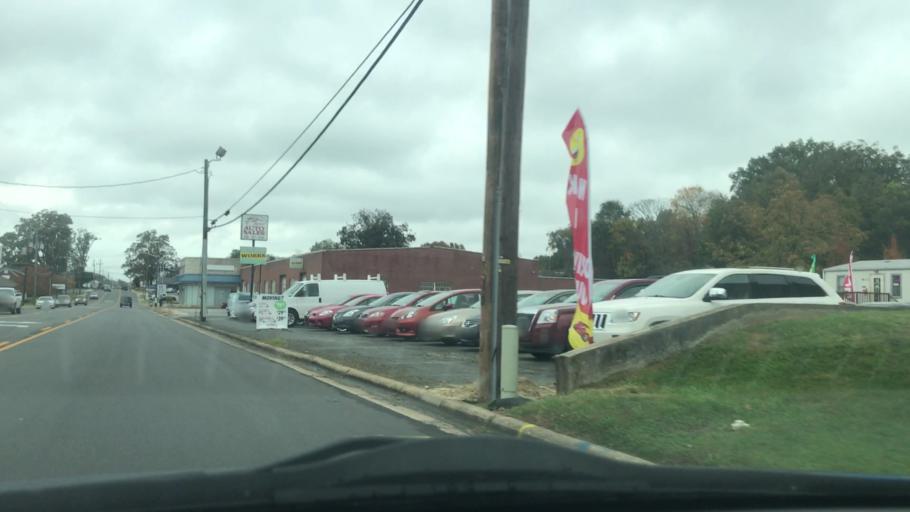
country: US
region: North Carolina
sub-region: Randolph County
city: Asheboro
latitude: 35.6942
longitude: -79.8155
